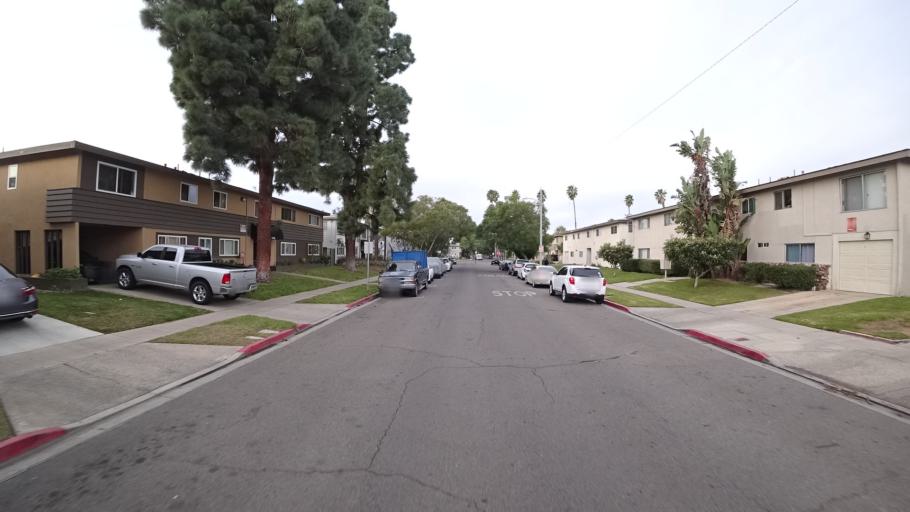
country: US
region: California
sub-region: Orange County
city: Garden Grove
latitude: 33.7730
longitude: -117.9237
